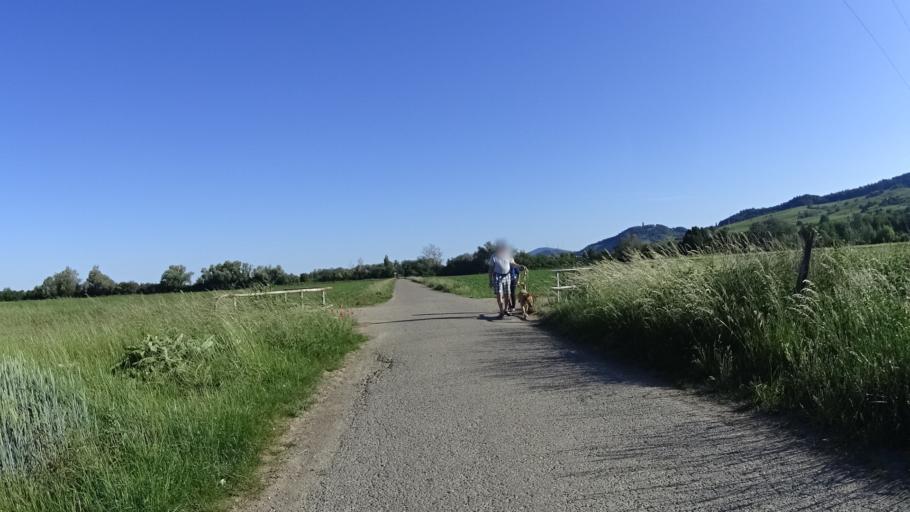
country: DE
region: Baden-Wuerttemberg
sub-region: Karlsruhe Region
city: Laudenbach
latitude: 49.6160
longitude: 8.6397
